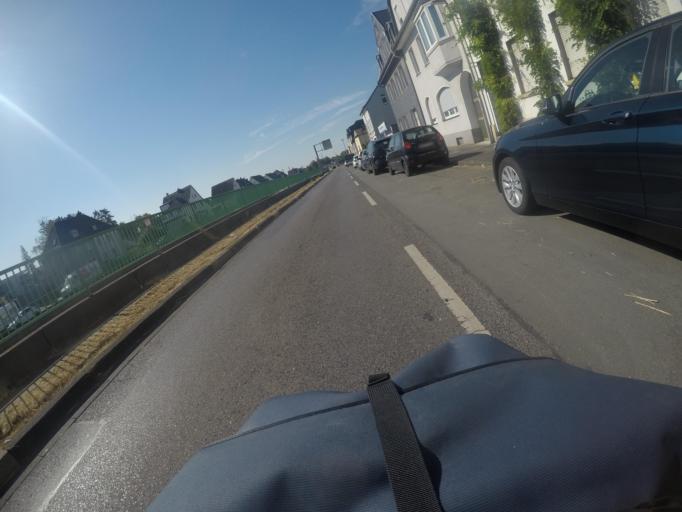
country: DE
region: North Rhine-Westphalia
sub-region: Regierungsbezirk Koln
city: Leverkusen
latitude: 51.0454
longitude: 6.9935
